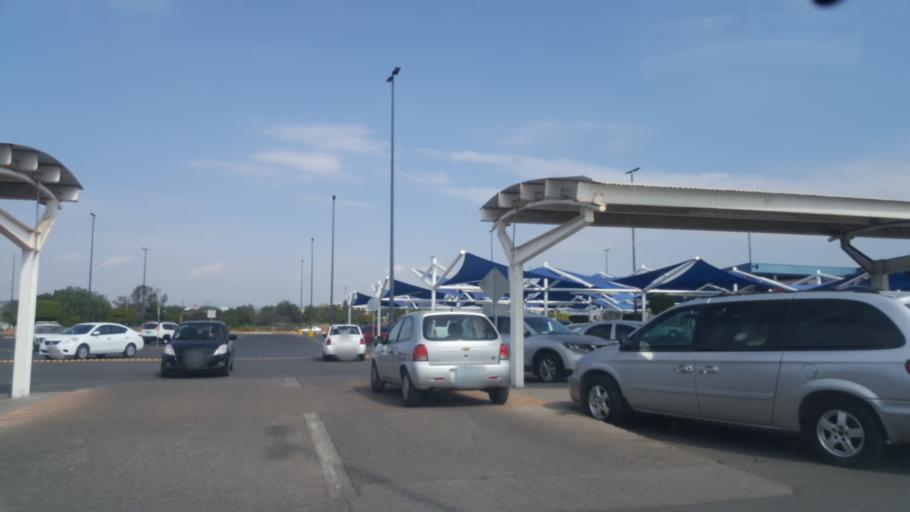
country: MX
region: Guanajuato
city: Leon
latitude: 21.0986
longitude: -101.6613
